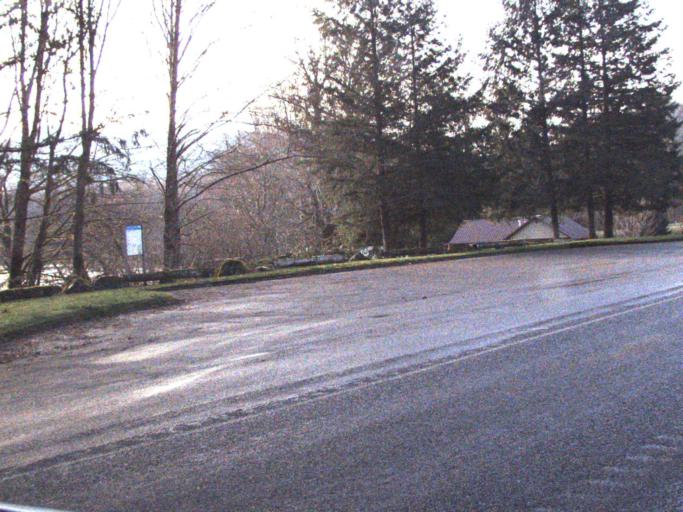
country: US
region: Washington
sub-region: Snohomish County
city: Darrington
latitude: 48.5352
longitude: -121.7348
